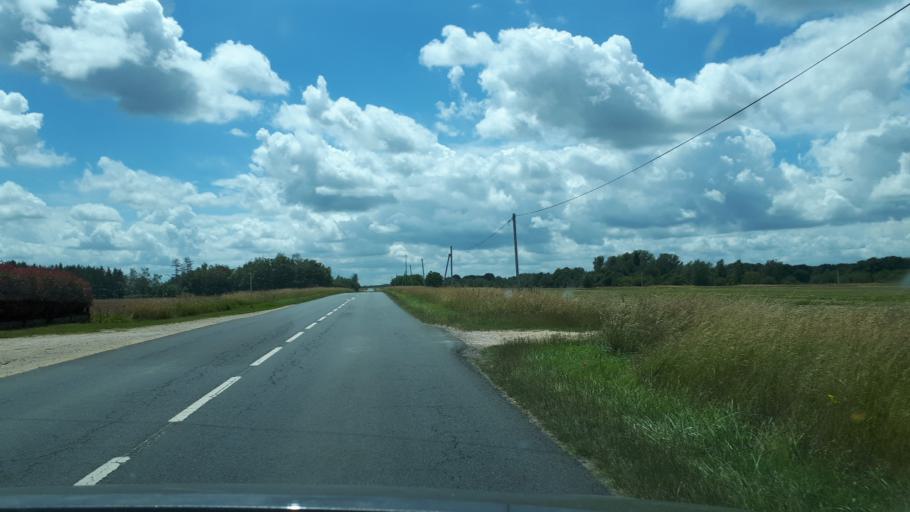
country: FR
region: Centre
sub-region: Departement du Loir-et-Cher
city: Contres
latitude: 47.4029
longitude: 1.4160
